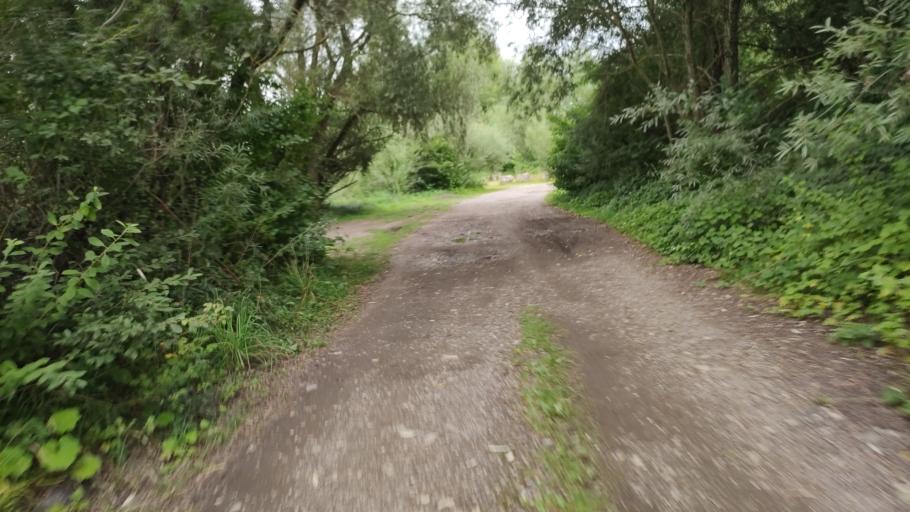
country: DE
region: Bavaria
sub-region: Swabia
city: Konigsbrunn
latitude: 48.2450
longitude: 10.8872
